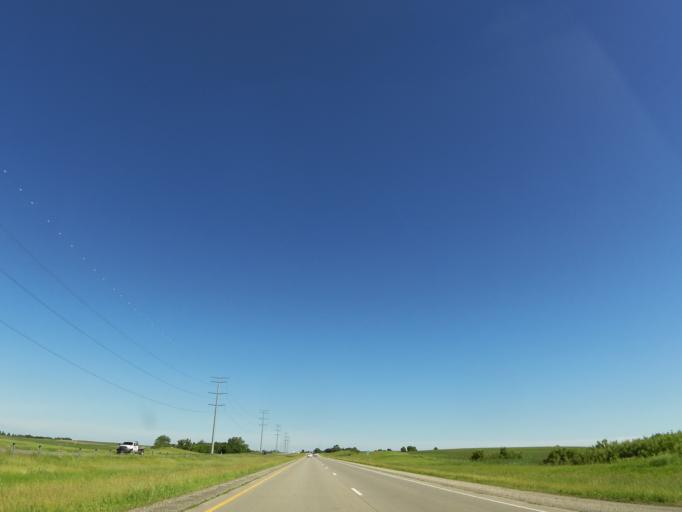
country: US
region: Minnesota
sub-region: Otter Tail County
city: Fergus Falls
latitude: 46.4139
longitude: -96.2128
